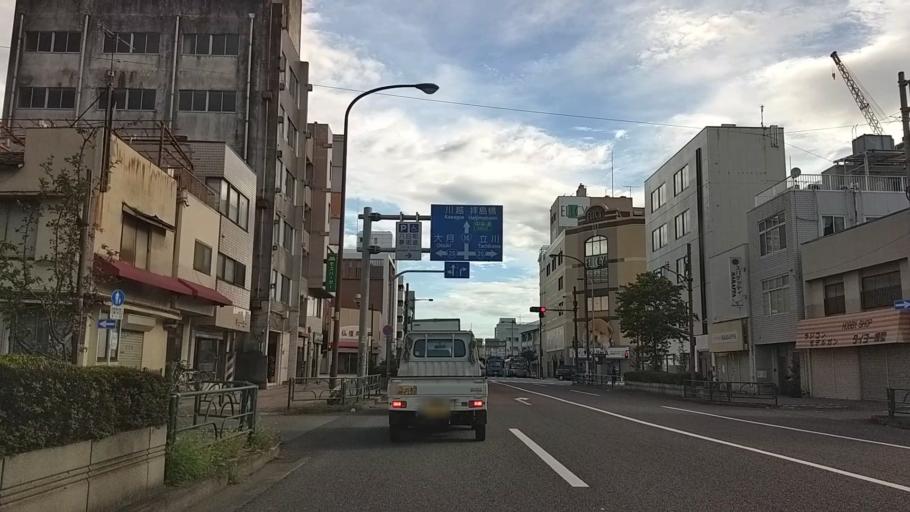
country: JP
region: Tokyo
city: Hachioji
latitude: 35.6597
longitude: 139.3286
